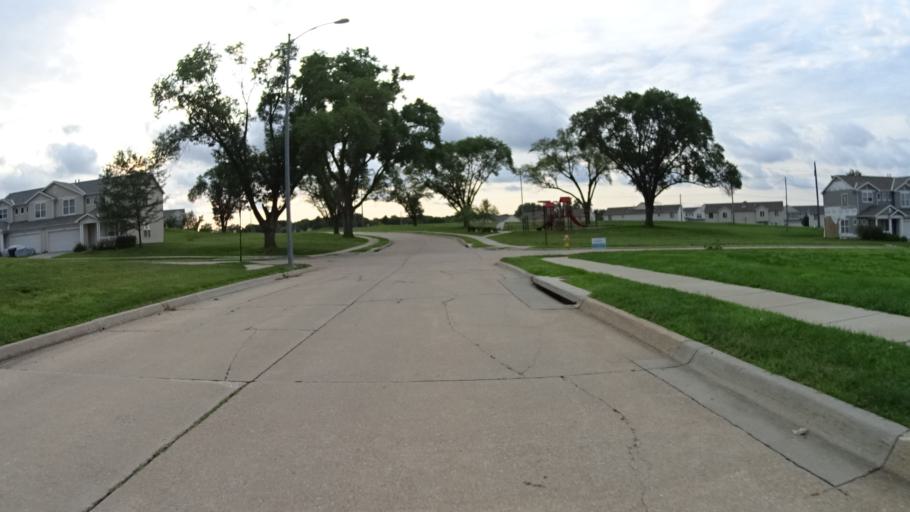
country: US
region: Nebraska
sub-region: Sarpy County
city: Offutt Air Force Base
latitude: 41.1245
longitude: -95.9519
